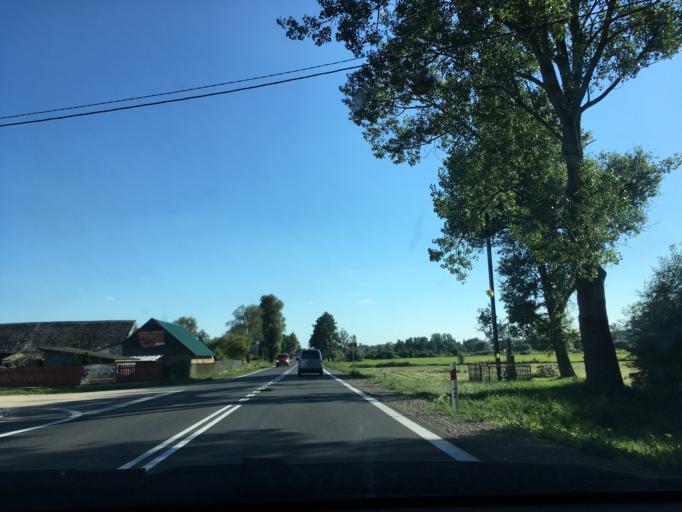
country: PL
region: Podlasie
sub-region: Powiat sokolski
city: Suchowola
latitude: 53.4620
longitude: 23.0886
